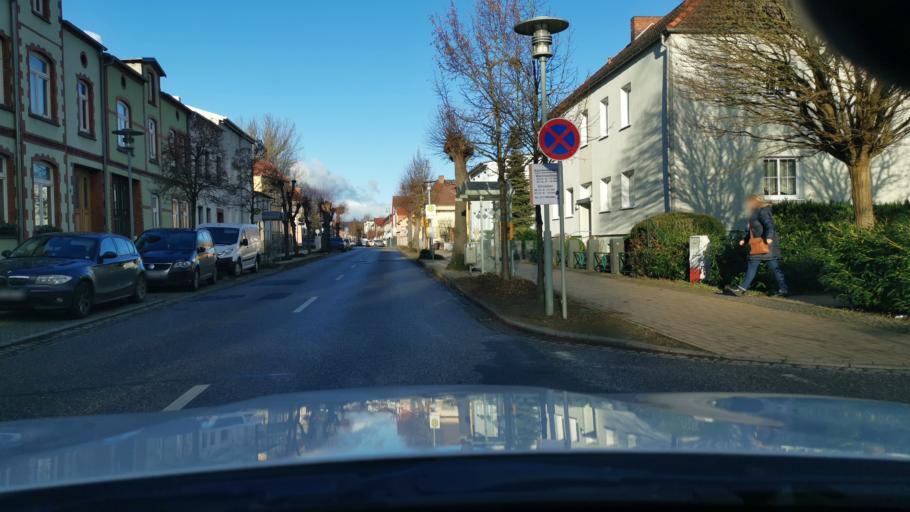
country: DE
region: Mecklenburg-Vorpommern
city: Tessin
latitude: 54.0276
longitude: 12.4614
